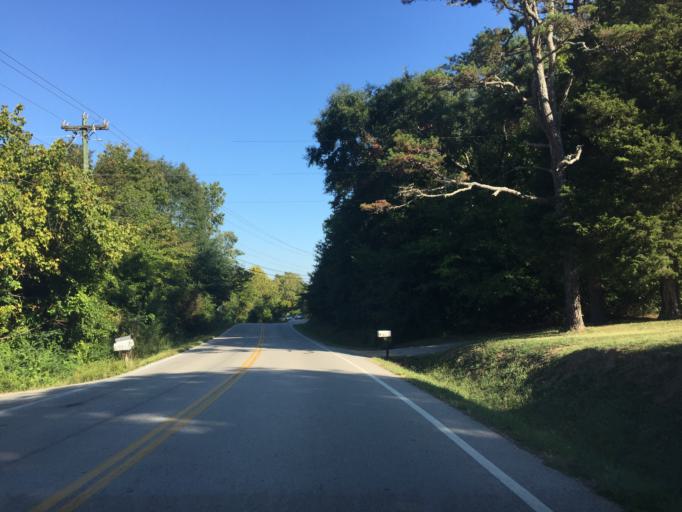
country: US
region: Tennessee
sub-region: Hamilton County
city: Harrison
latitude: 35.1181
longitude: -85.0830
